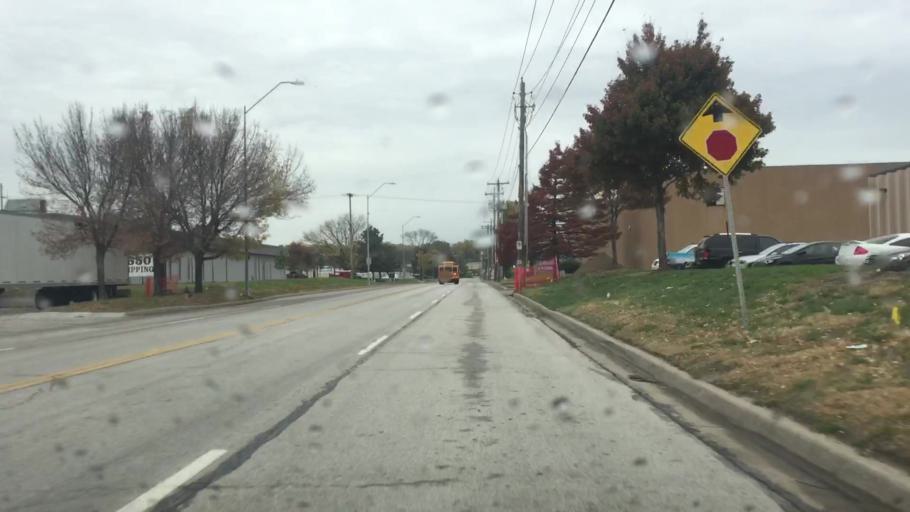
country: US
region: Missouri
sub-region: Clay County
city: North Kansas City
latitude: 39.1381
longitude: -94.5138
